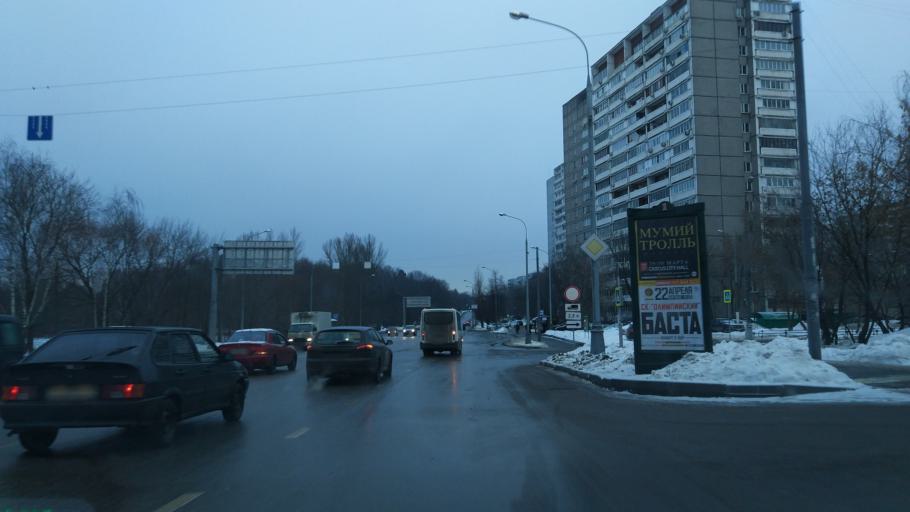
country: RU
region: Moscow
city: Ivanovskoye
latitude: 55.7724
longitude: 37.8200
